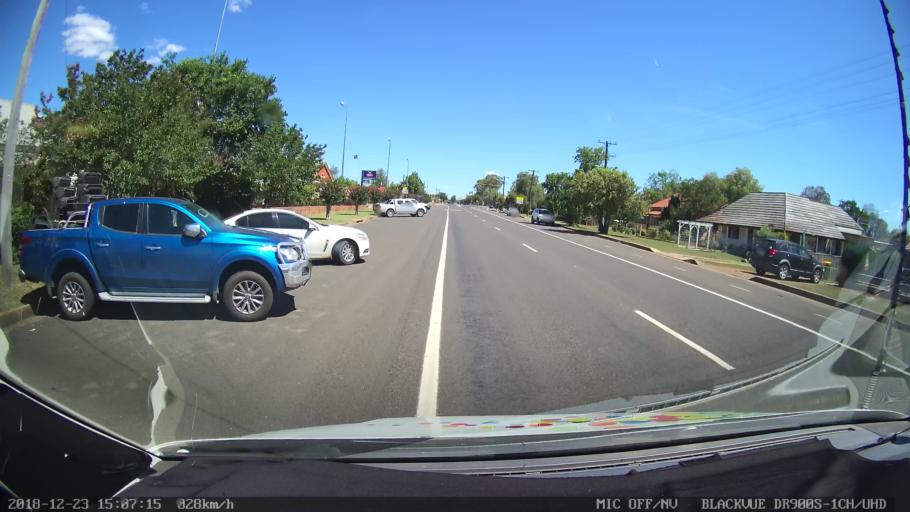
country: AU
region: New South Wales
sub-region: Tamworth Municipality
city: Manilla
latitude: -30.7470
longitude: 150.7242
